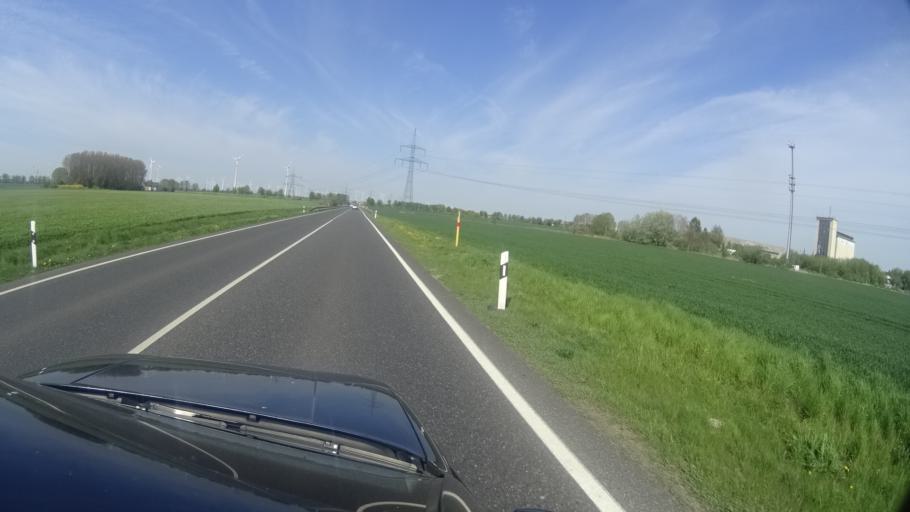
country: DE
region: Brandenburg
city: Nauen
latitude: 52.5924
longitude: 12.8847
